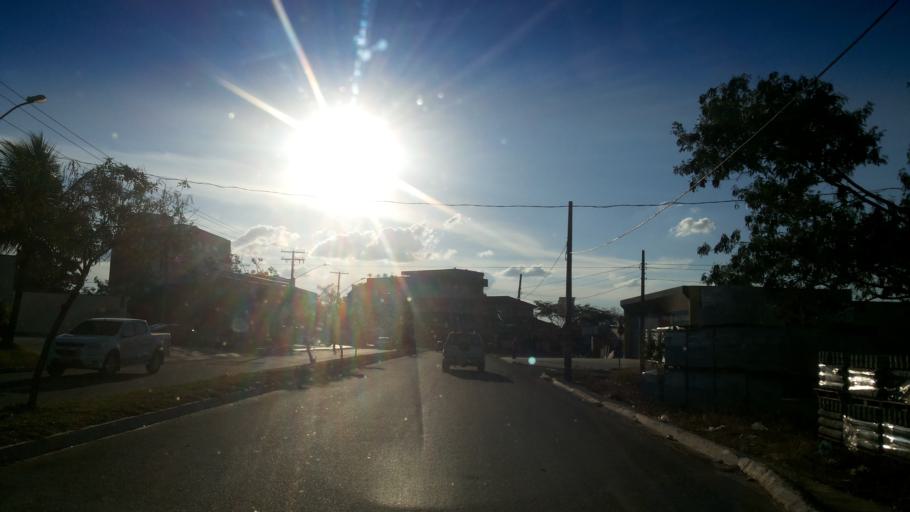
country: BR
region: Goias
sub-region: Goiania
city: Goiania
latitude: -16.7262
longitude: -49.3029
